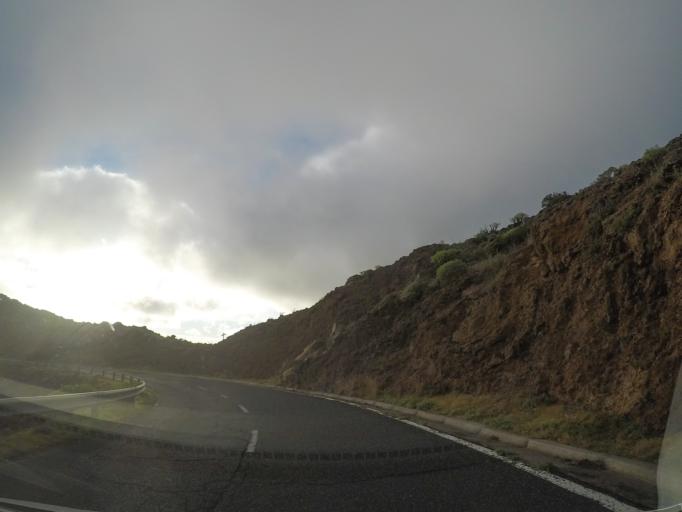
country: ES
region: Canary Islands
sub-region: Provincia de Santa Cruz de Tenerife
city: Alajero
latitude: 28.0898
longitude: -17.2550
